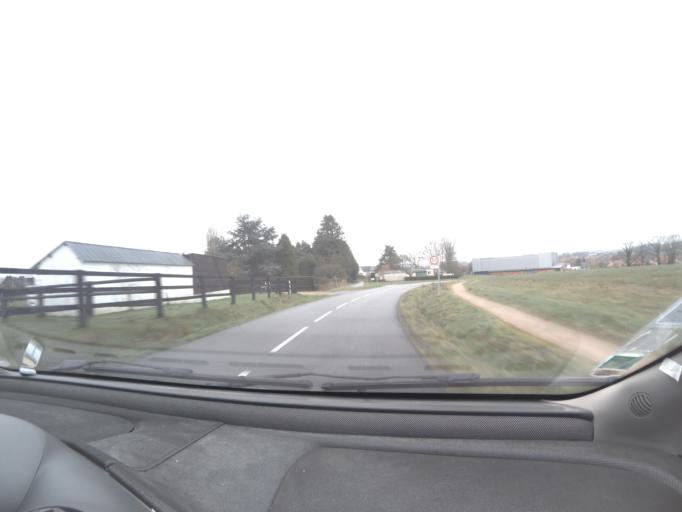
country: FR
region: Pays de la Loire
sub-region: Departement de la Sarthe
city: Saint-Saturnin
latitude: 48.0576
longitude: 0.1453
